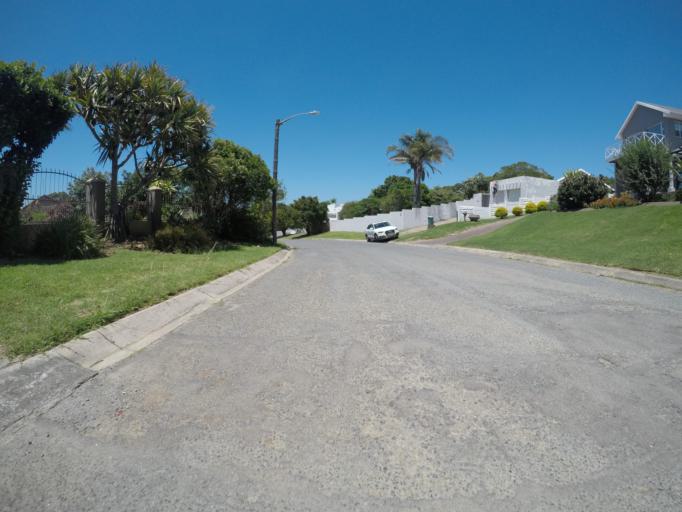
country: ZA
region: Eastern Cape
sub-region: Buffalo City Metropolitan Municipality
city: East London
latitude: -32.9610
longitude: 27.9589
